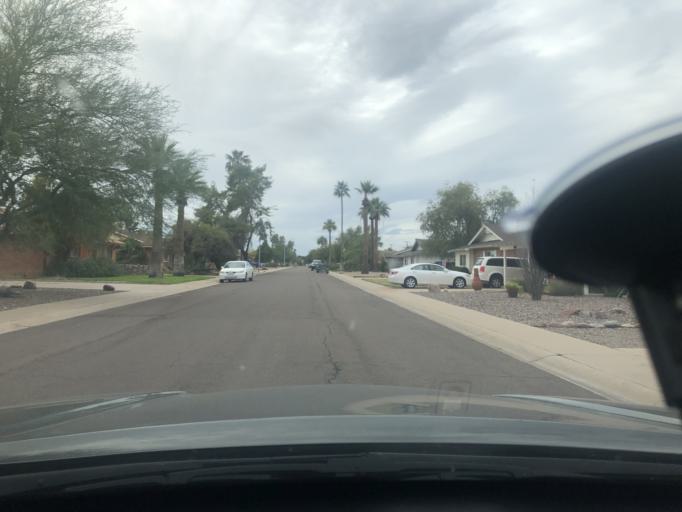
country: US
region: Arizona
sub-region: Maricopa County
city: Scottsdale
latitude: 33.4775
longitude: -111.8967
